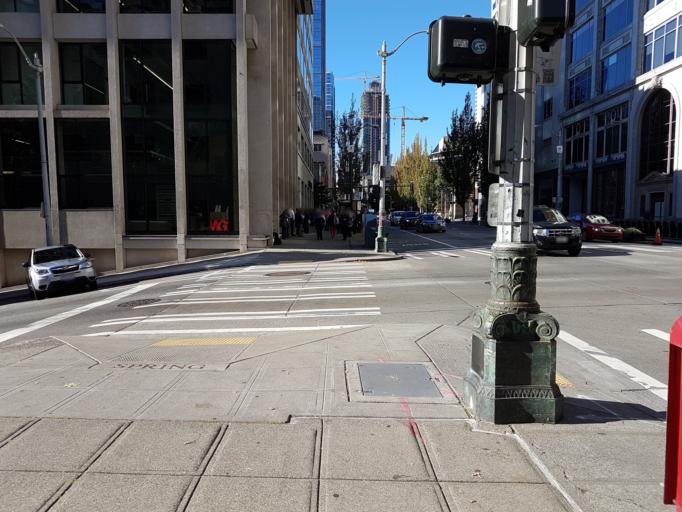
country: US
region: Washington
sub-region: King County
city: Seattle
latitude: 47.6053
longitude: -122.3351
